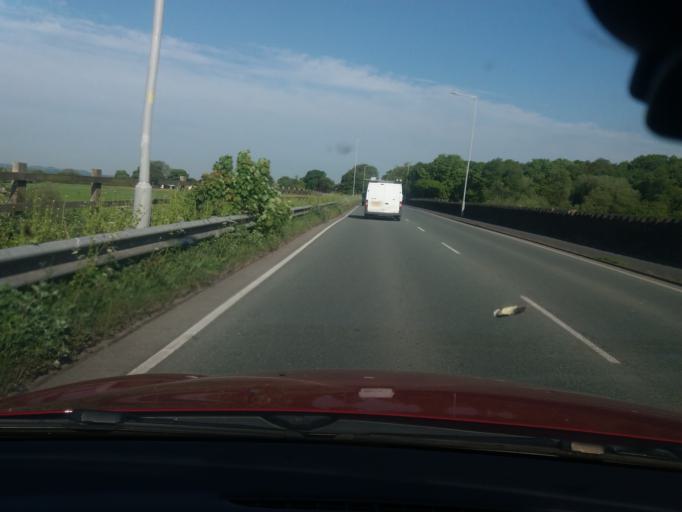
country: GB
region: England
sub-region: Borough of Wigan
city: Haigh
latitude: 53.6087
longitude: -2.5703
